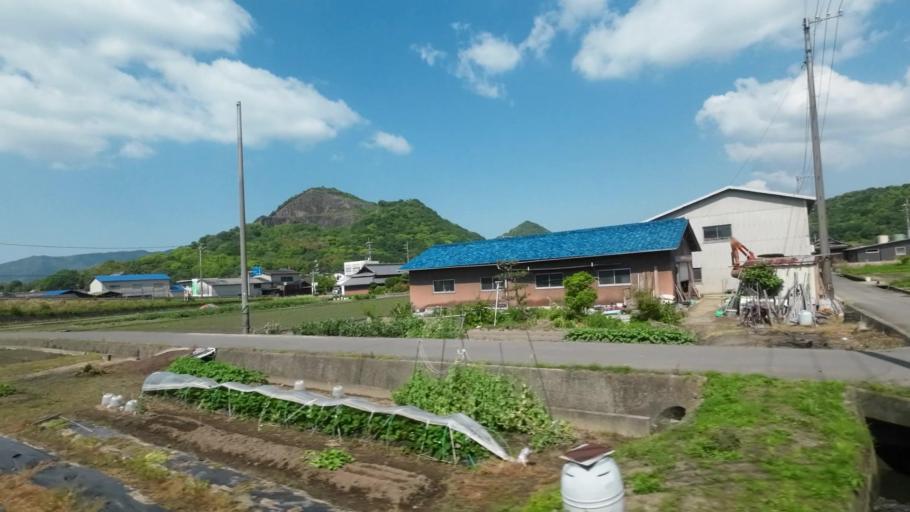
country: JP
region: Kagawa
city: Kan'onjicho
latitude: 34.1891
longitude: 133.7130
